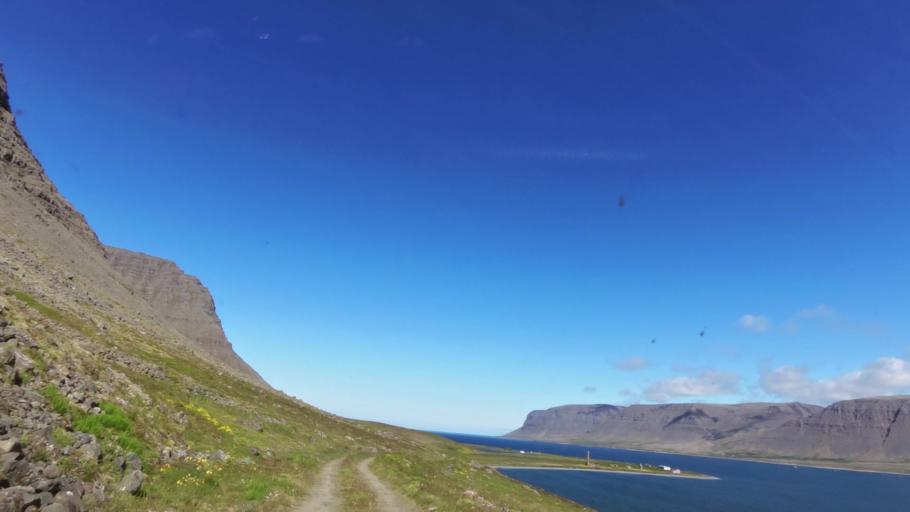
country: IS
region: West
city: Olafsvik
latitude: 65.6344
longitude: -23.9243
